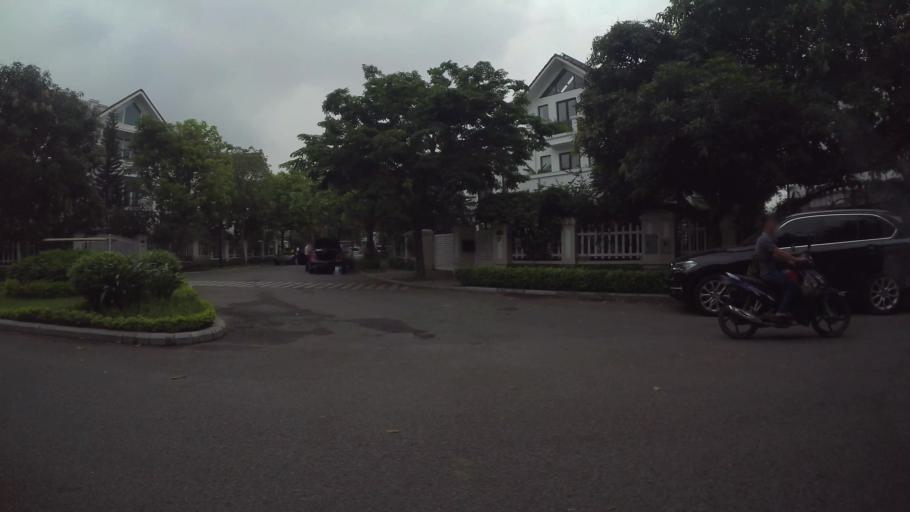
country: VN
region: Ha Noi
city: Trau Quy
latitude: 21.0505
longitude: 105.9135
